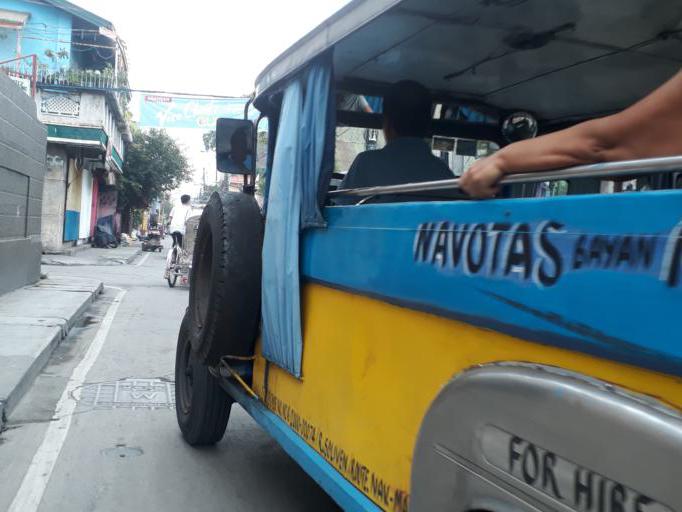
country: PH
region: Calabarzon
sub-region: Province of Rizal
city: Malabon
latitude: 14.6709
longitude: 120.9382
